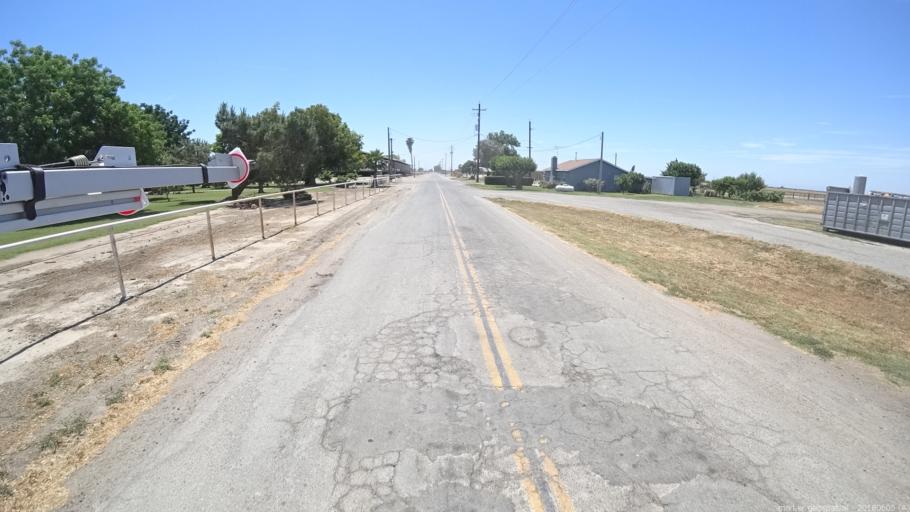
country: US
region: California
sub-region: Madera County
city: Chowchilla
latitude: 37.0913
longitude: -120.3289
